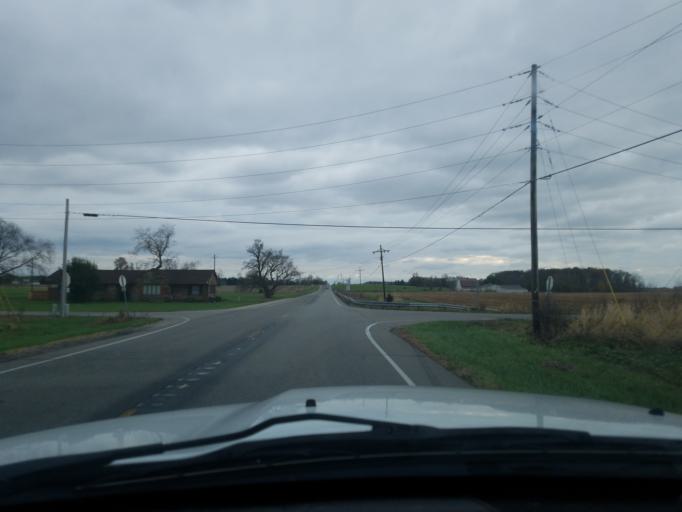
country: US
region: Indiana
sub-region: Bartholomew County
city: Hope
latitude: 39.2693
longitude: -85.7715
